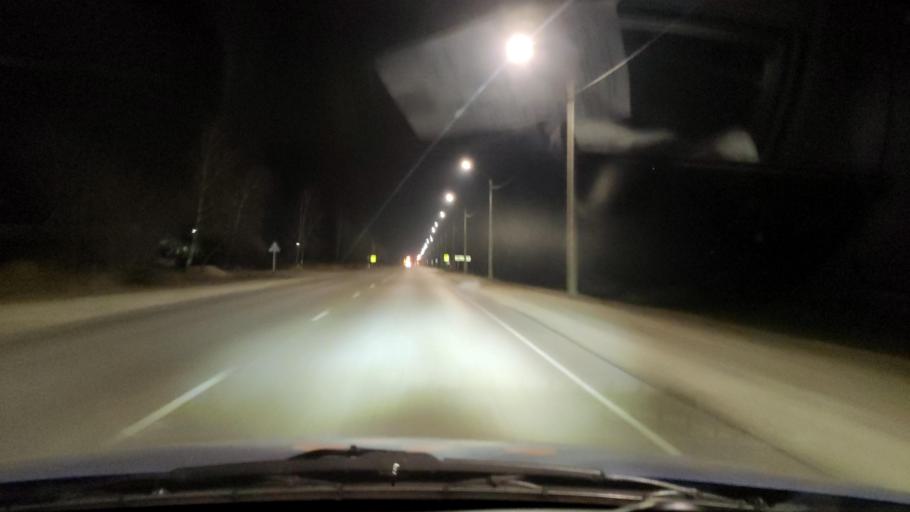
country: RU
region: Voronezj
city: Semiluki
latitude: 51.7131
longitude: 39.0275
